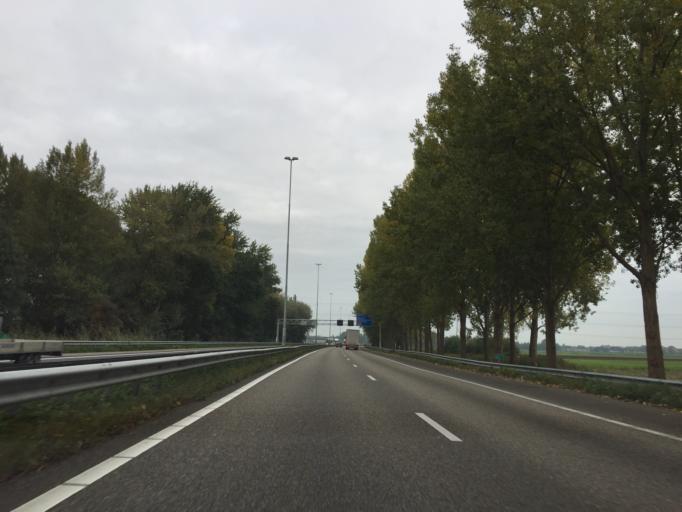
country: NL
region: North Brabant
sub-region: Gemeente Oosterhout
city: Oosterhout
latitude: 51.6695
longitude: 4.8798
